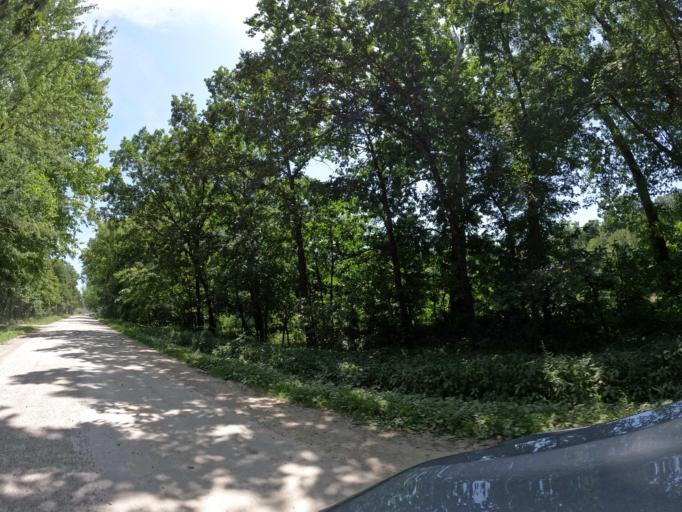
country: US
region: Iowa
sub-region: Henry County
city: Mount Pleasant
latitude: 40.9338
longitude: -91.6105
